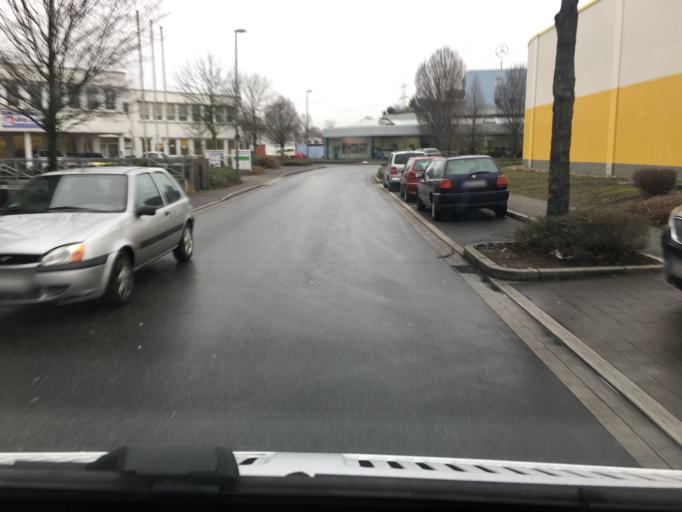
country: DE
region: North Rhine-Westphalia
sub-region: Regierungsbezirk Dusseldorf
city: Dormagen
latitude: 51.0926
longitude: 6.8126
